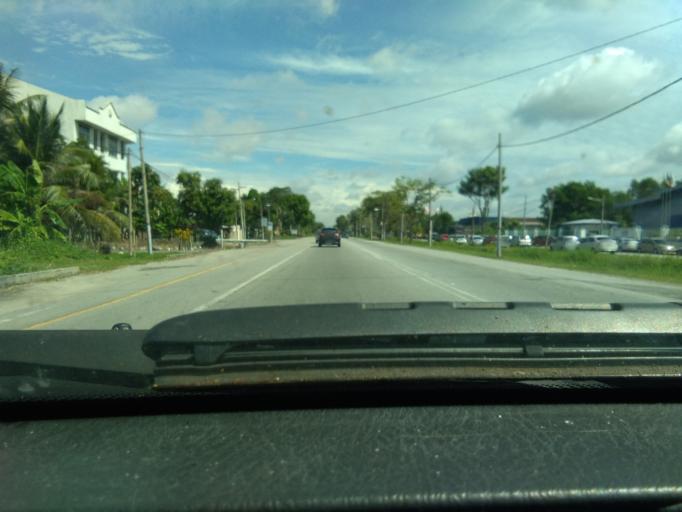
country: MY
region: Perak
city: Parit Buntar
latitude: 5.1034
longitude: 100.4862
